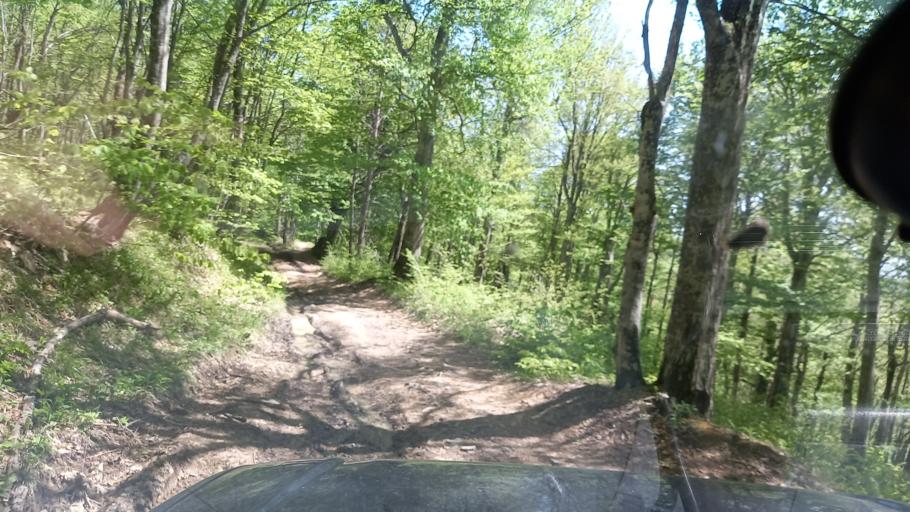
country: RU
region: Krasnodarskiy
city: Tuapse
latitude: 44.2470
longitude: 39.2902
